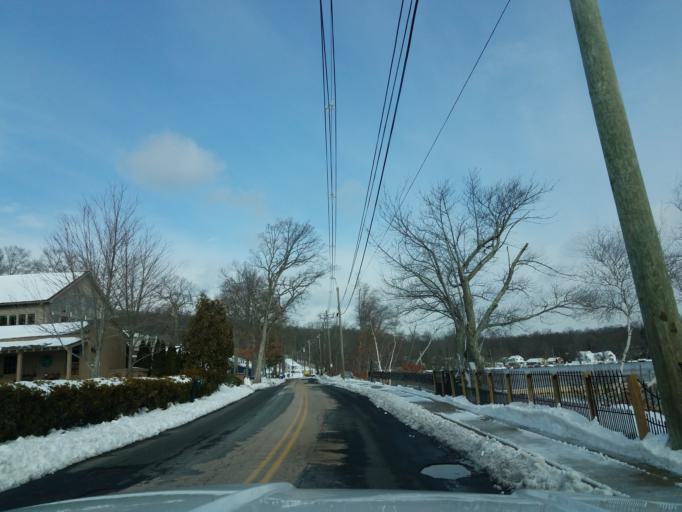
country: US
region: Connecticut
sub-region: Middlesex County
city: Lake Pocotopaug
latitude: 41.5989
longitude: -72.5103
